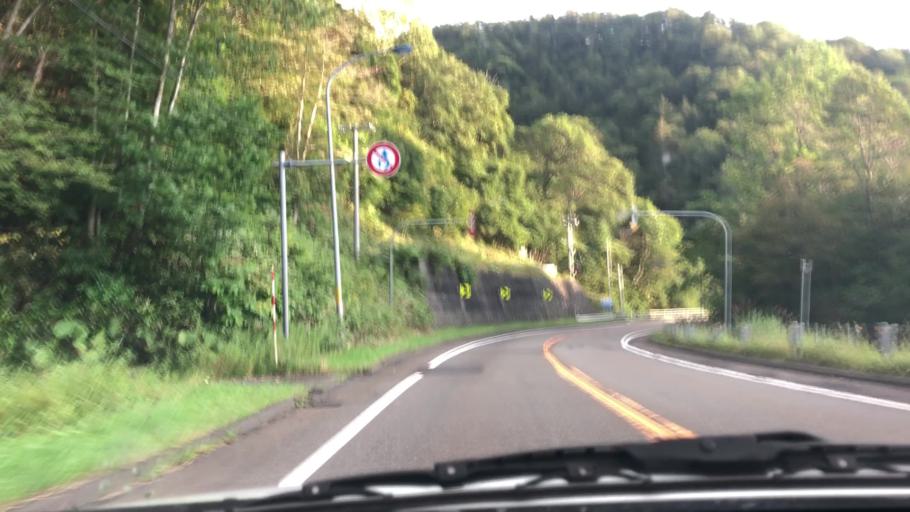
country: JP
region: Hokkaido
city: Shimo-furano
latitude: 42.8904
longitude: 142.2988
